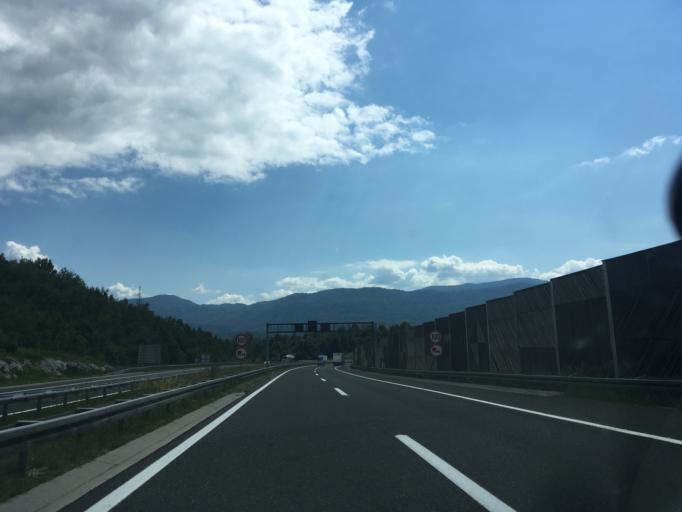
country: HR
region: Primorsko-Goranska
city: Vrbovsko
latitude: 45.3710
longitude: 15.0961
